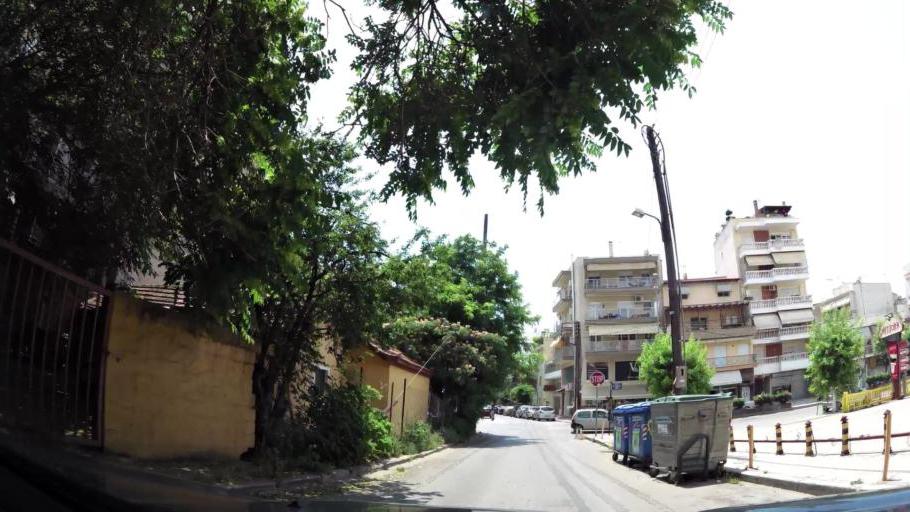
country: GR
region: Central Macedonia
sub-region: Nomos Thessalonikis
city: Ampelokipoi
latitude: 40.6562
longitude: 22.9279
